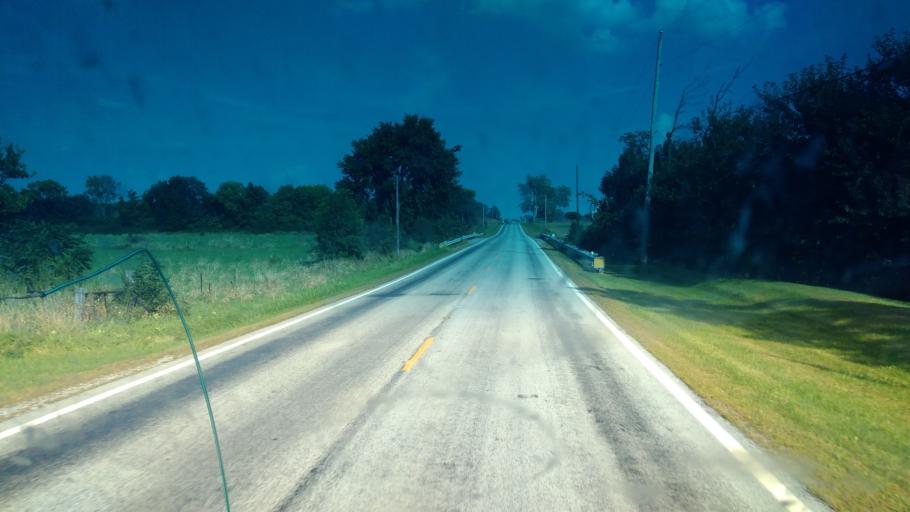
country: US
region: Ohio
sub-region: Hardin County
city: Forest
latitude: 40.8910
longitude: -83.5502
